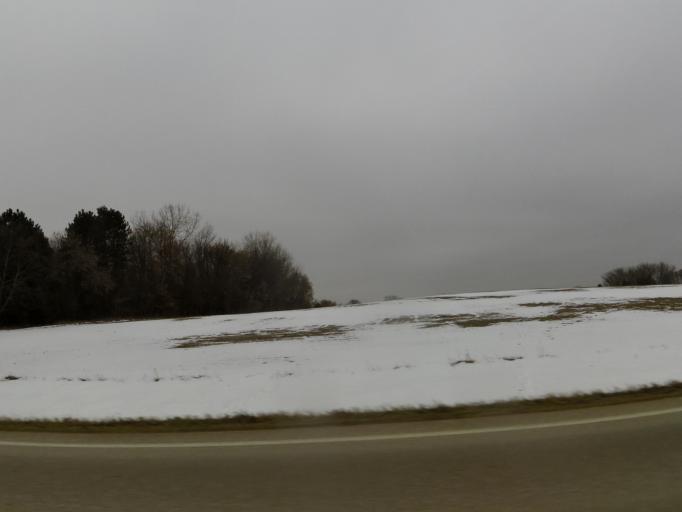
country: US
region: Minnesota
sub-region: Carver County
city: Carver
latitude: 44.7179
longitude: -93.6655
